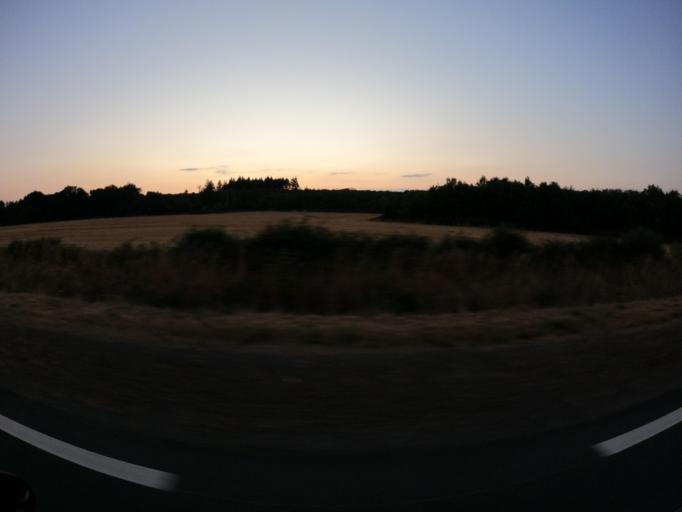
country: FR
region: Pays de la Loire
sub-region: Departement de Maine-et-Loire
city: Freigne
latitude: 47.4950
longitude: -1.1333
